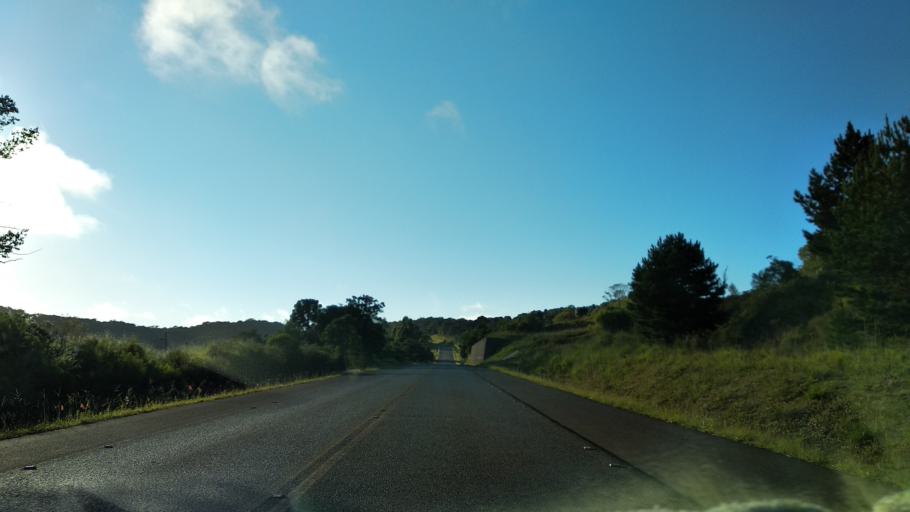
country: BR
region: Santa Catarina
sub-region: Correia Pinto
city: Correia Pinto
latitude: -27.6147
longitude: -50.6902
